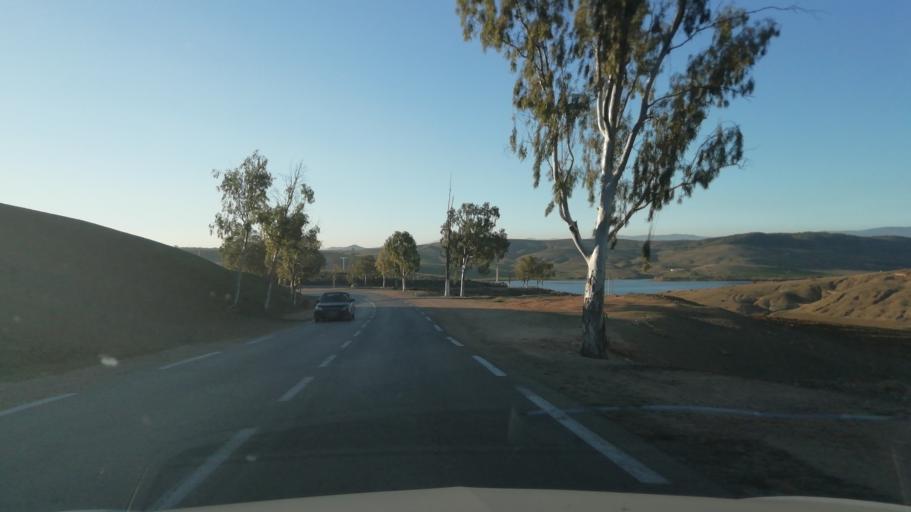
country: DZ
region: Tlemcen
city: Nedroma
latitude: 34.8284
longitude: -1.6449
